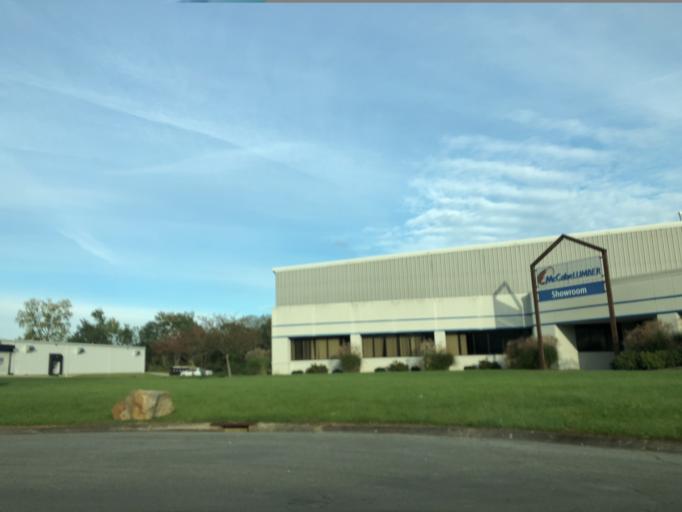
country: US
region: Ohio
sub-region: Hamilton County
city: Sixteen Mile Stand
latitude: 39.2808
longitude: -84.2996
